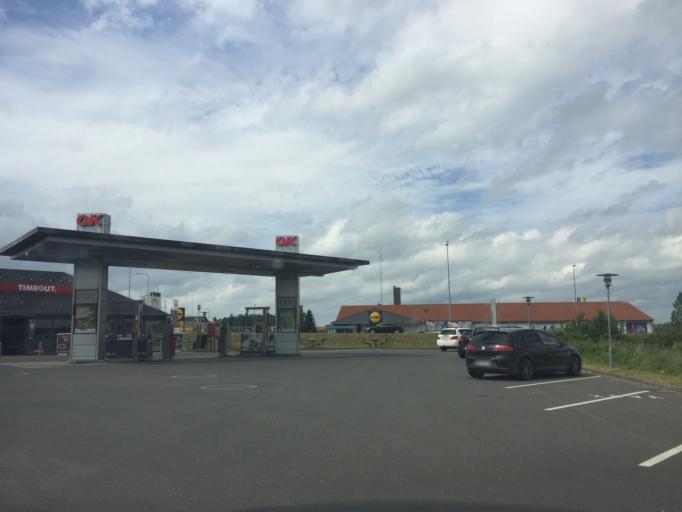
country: DK
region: South Denmark
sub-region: Faaborg-Midtfyn Kommune
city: Ringe
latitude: 55.2356
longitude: 10.4901
